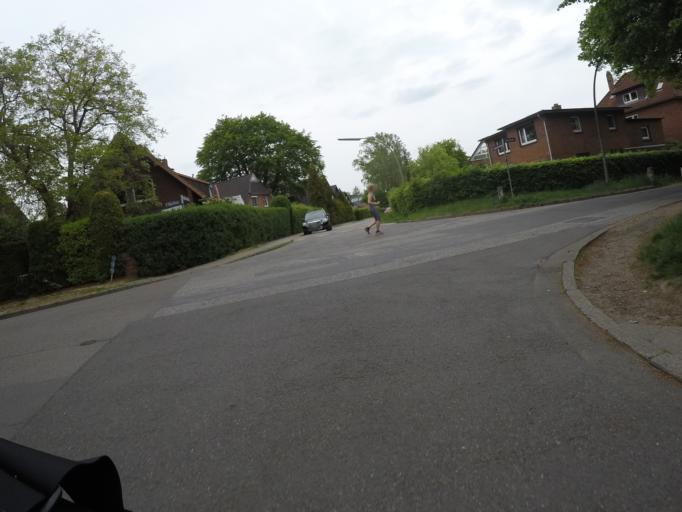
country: DE
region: Hamburg
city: Hamburg-Nord
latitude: 53.6223
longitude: 9.9587
